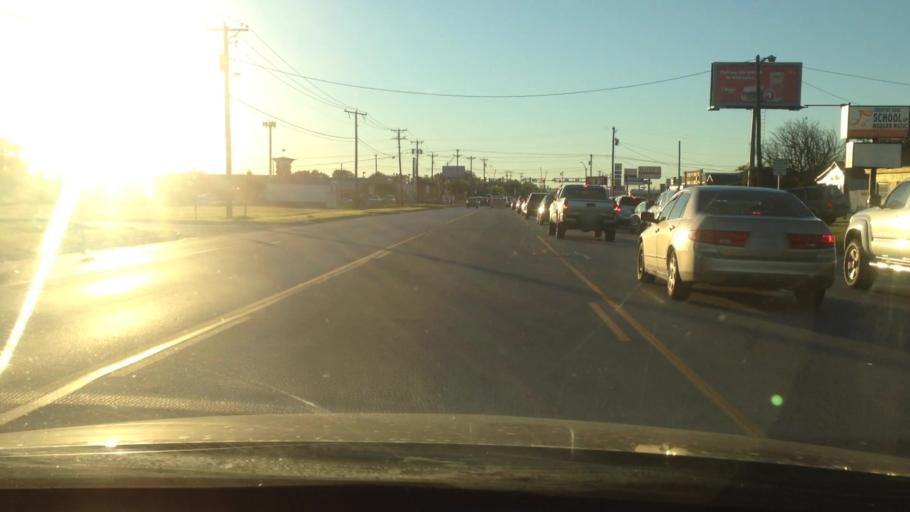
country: US
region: Texas
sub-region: Tarrant County
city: Watauga
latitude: 32.8605
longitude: -97.2615
